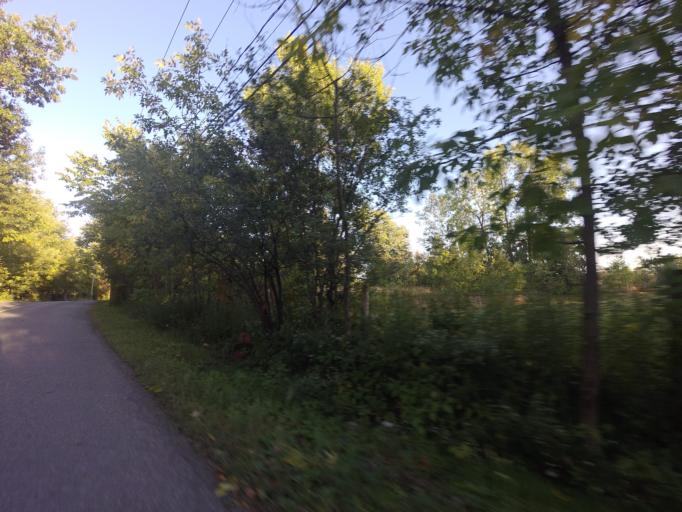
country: CA
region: Quebec
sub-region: Monteregie
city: Hudson
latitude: 45.4831
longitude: -74.2095
